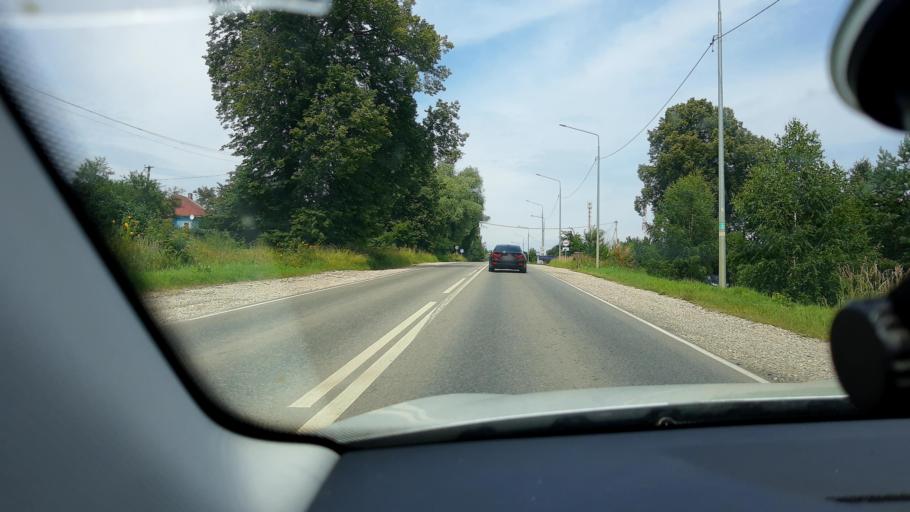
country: RU
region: Tula
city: Zaokskiy
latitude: 54.7589
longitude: 37.4375
